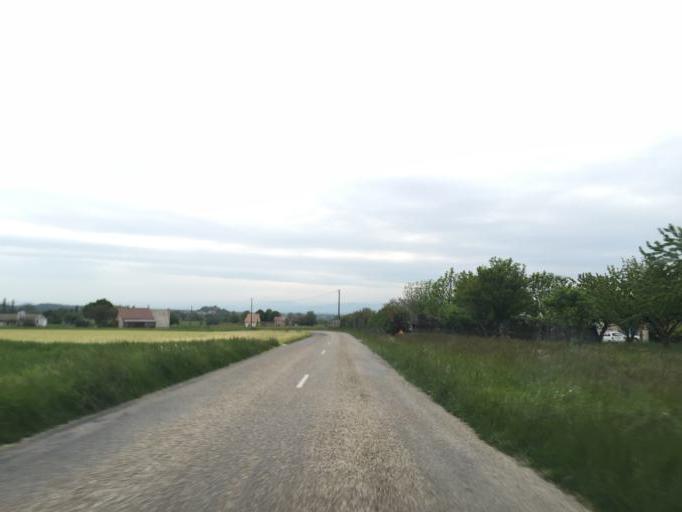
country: FR
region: Rhone-Alpes
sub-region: Departement de la Drome
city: Chatuzange-le-Goubet
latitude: 44.9505
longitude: 5.1172
